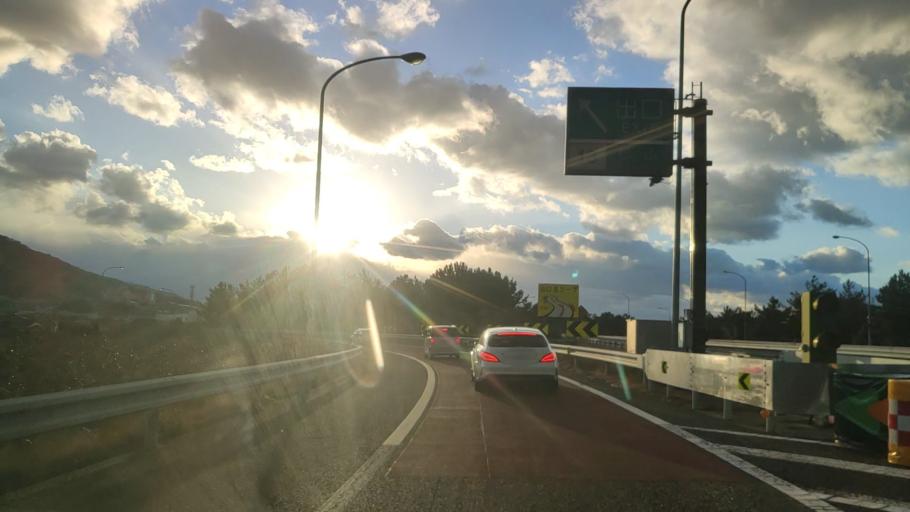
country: JP
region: Ehime
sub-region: Shikoku-chuo Shi
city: Matsuyama
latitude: 33.7956
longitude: 132.7832
